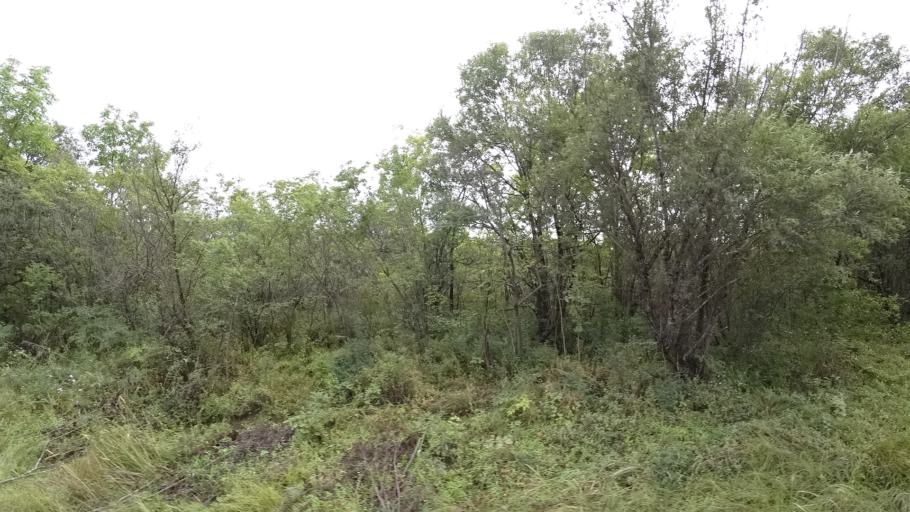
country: RU
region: Primorskiy
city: Lyalichi
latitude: 44.0764
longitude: 132.4580
